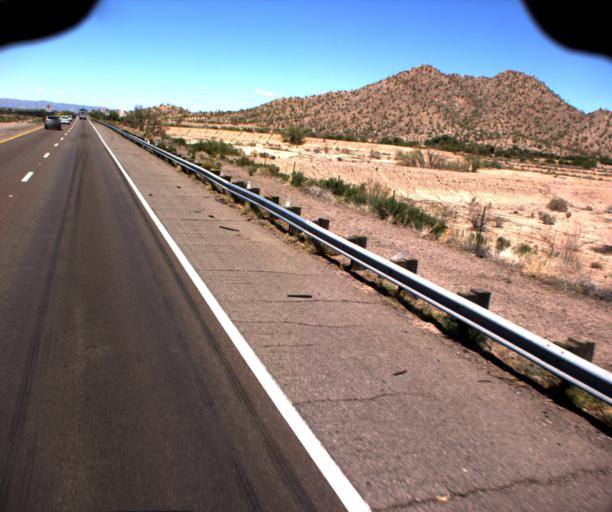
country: US
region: Arizona
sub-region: Pinal County
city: Casa Blanca
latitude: 33.1454
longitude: -111.8630
